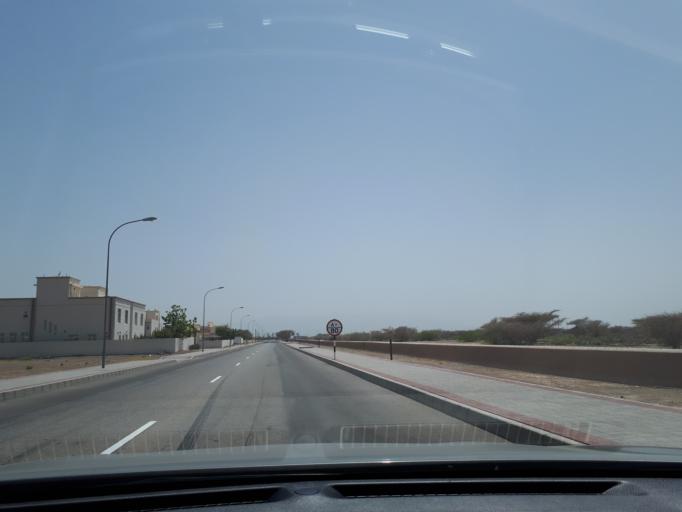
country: OM
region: Muhafazat Masqat
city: As Sib al Jadidah
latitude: 23.6908
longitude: 58.1059
